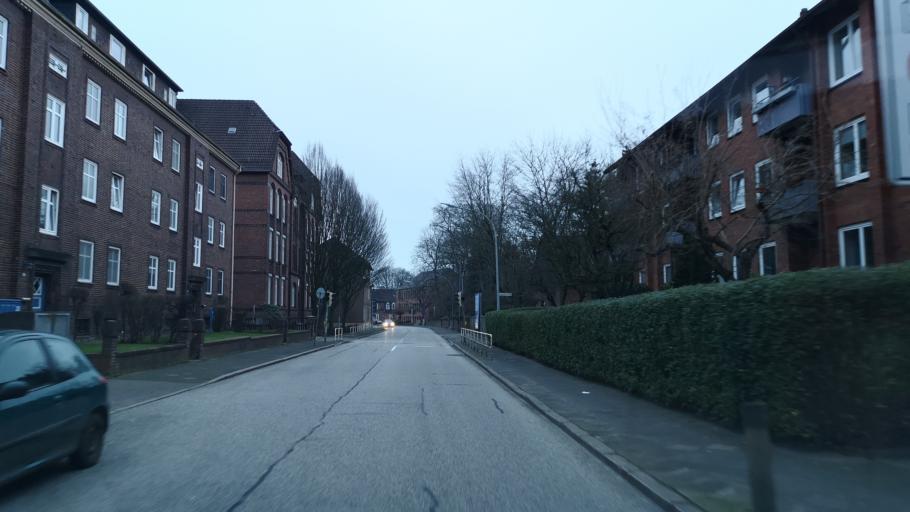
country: DE
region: Schleswig-Holstein
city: Itzehoe
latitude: 53.9247
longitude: 9.5284
